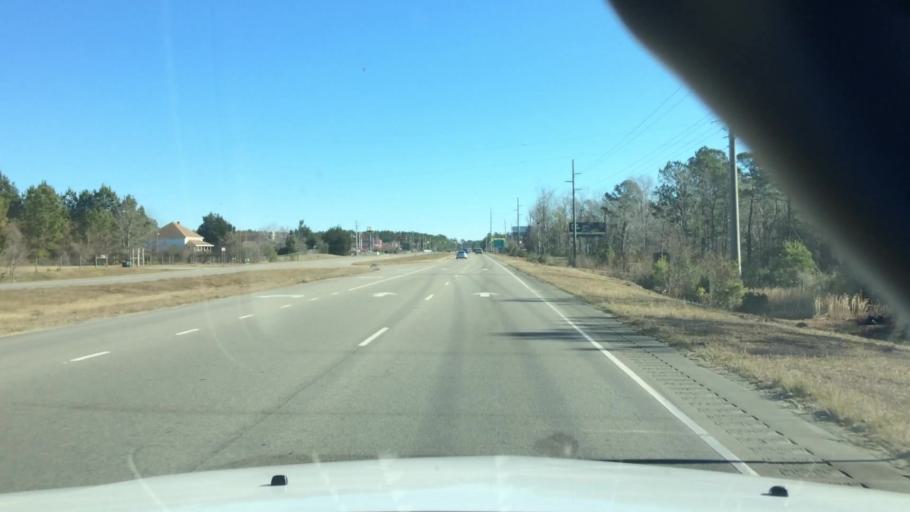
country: US
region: North Carolina
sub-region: Brunswick County
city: Shallotte
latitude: 34.0152
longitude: -78.2785
